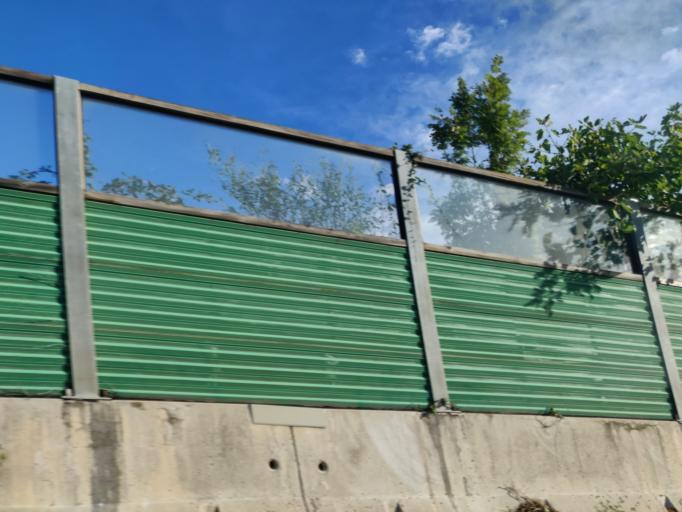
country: IT
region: Tuscany
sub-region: Provincia di Grosseto
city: Gavorrano
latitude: 42.9512
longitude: 10.9115
